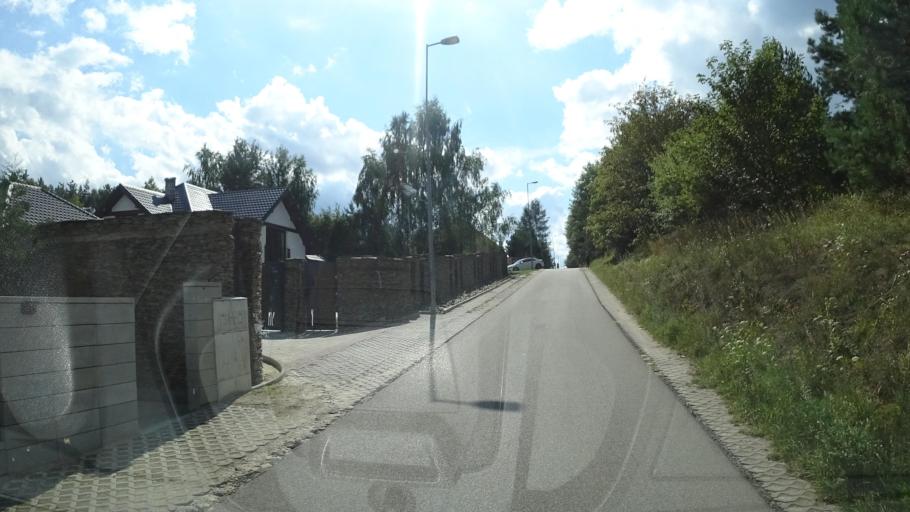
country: PL
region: Podlasie
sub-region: Powiat lomzynski
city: Piatnica
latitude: 53.1400
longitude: 22.1238
